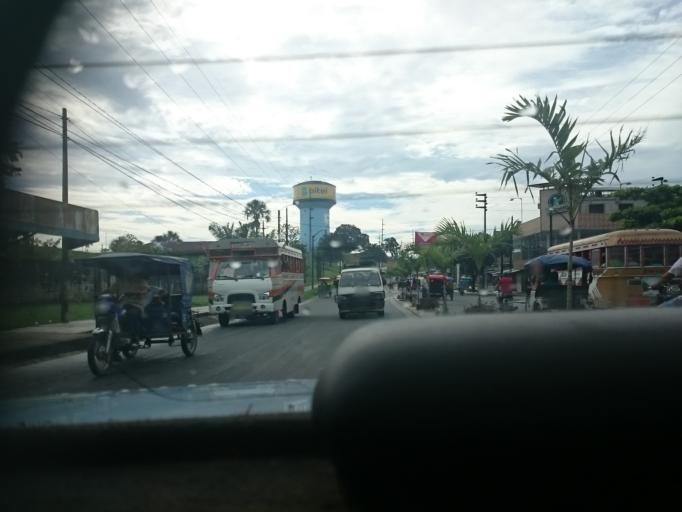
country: PE
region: Loreto
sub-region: Provincia de Maynas
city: Iquitos
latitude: -3.7650
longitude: -73.2599
